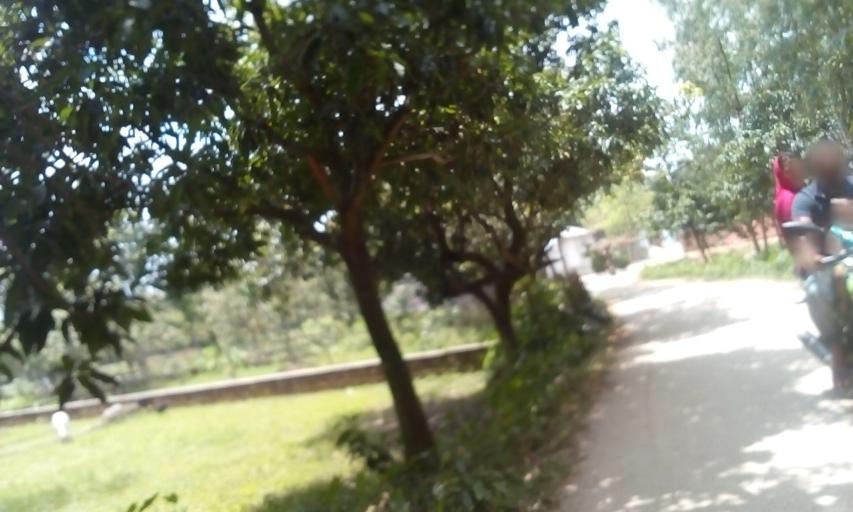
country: IN
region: West Bengal
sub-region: Dakshin Dinajpur
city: Balurghat
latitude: 25.3930
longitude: 88.9877
